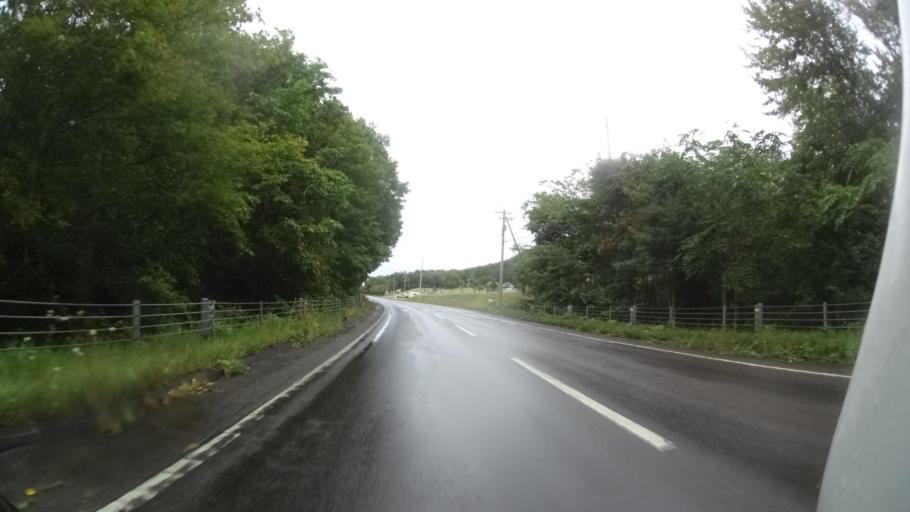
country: JP
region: Hokkaido
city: Kitami
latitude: 44.0996
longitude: 143.8201
